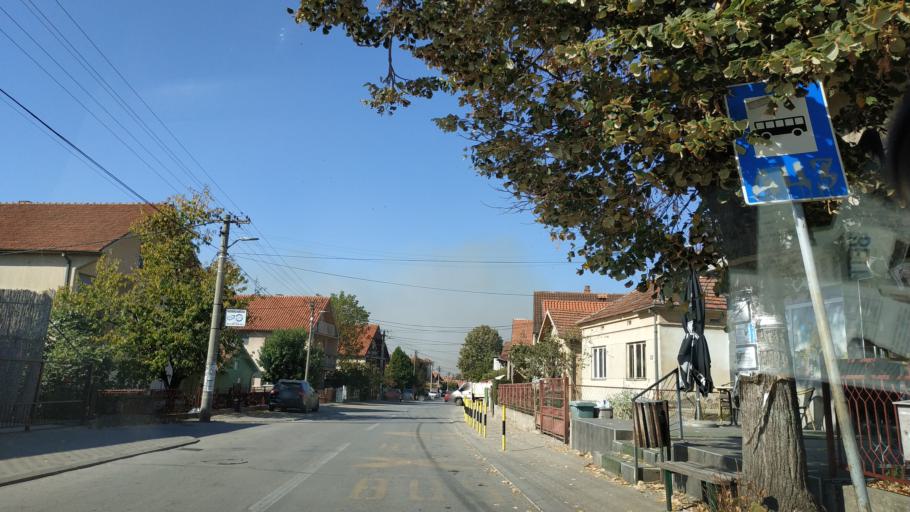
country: RS
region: Central Serbia
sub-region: Nisavski Okrug
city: Aleksinac
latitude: 43.5411
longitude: 21.6961
